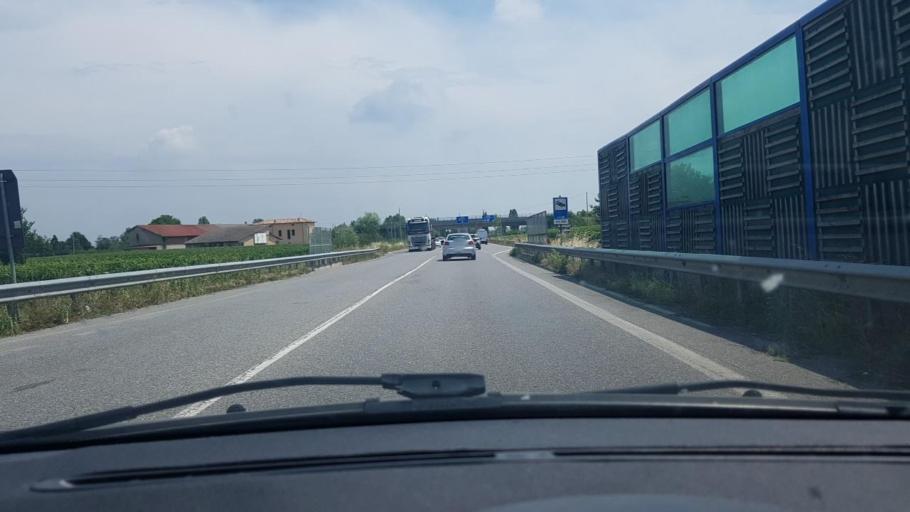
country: IT
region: Lombardy
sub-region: Provincia di Brescia
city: San Martino della Battaglia
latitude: 45.4444
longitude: 10.6136
